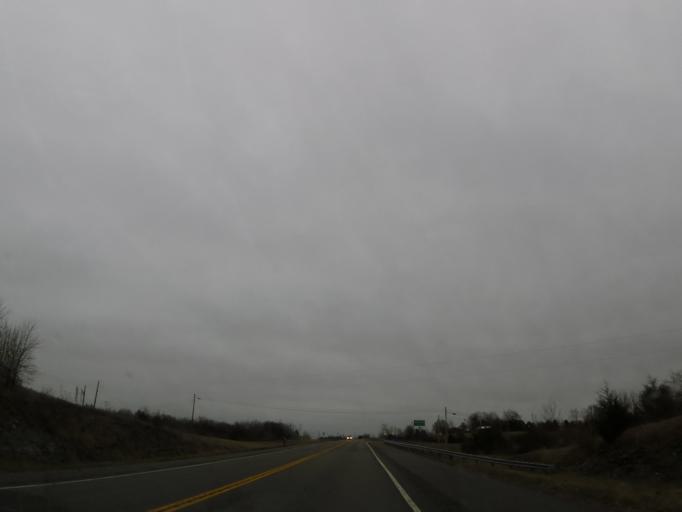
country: US
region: Kentucky
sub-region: Lincoln County
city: Stanford
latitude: 37.5211
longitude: -84.6185
